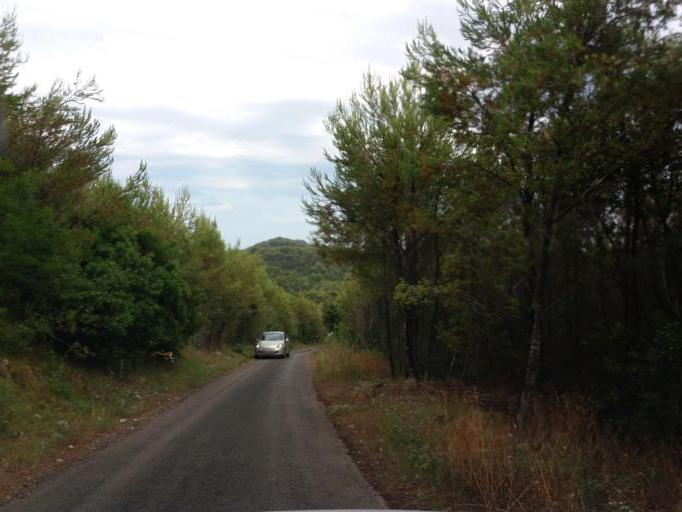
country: HR
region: Zadarska
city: Sali
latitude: 43.9109
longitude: 15.1281
